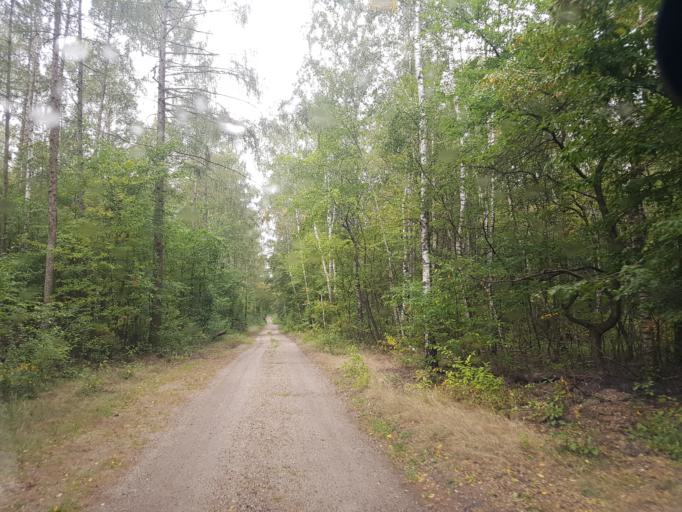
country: DE
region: Brandenburg
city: Trobitz
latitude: 51.5844
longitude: 13.4500
